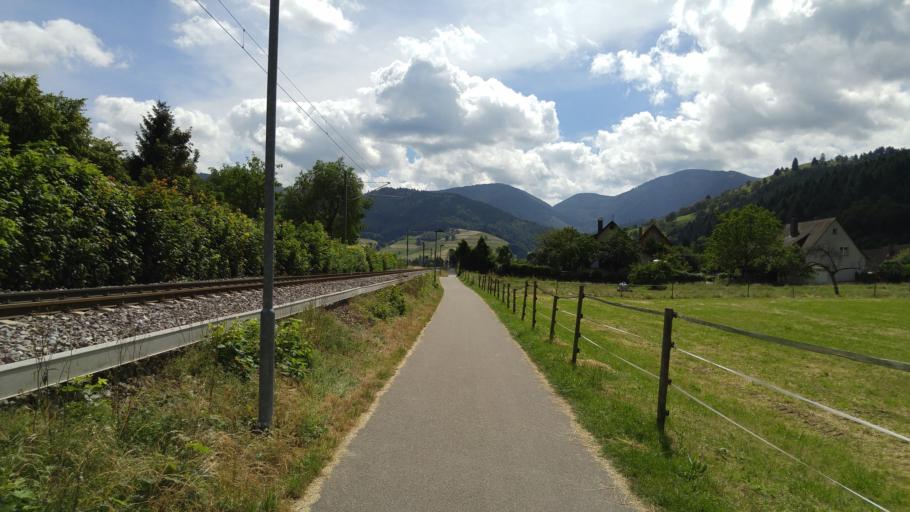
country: DE
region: Baden-Wuerttemberg
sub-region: Freiburg Region
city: Muenstertal/Schwarzwald
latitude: 47.8589
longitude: 7.7652
